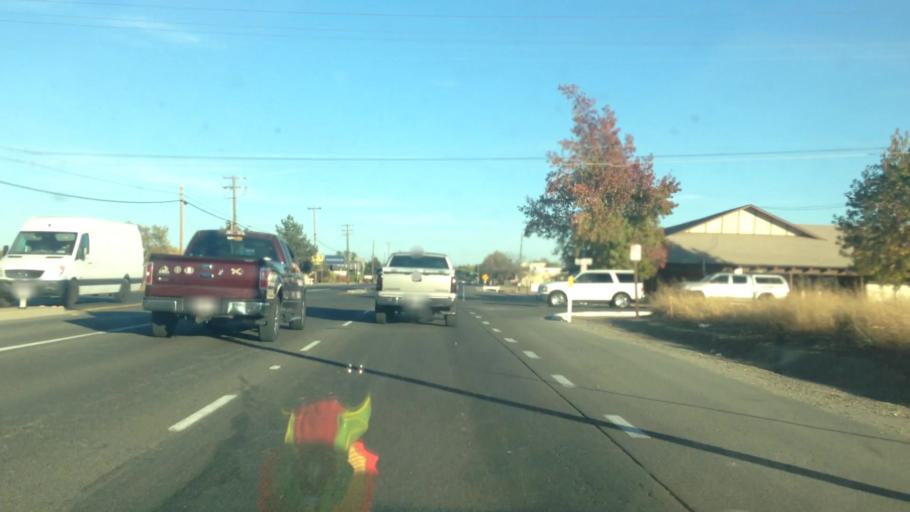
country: US
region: California
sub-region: Sacramento County
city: North Highlands
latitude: 38.6903
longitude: -121.3880
